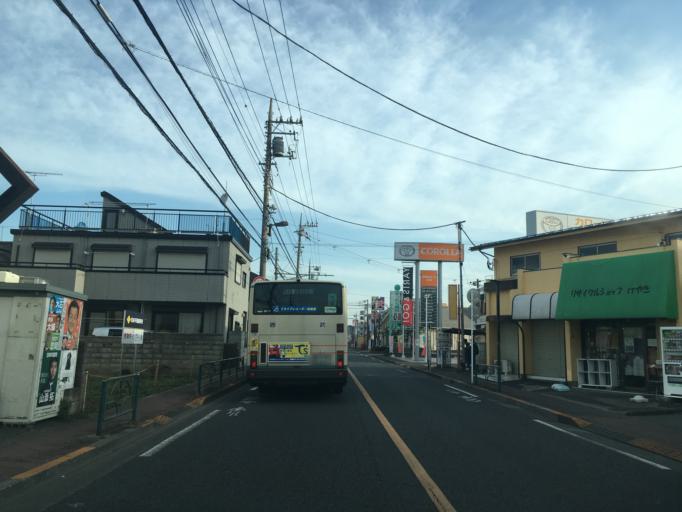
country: JP
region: Tokyo
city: Kokubunji
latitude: 35.7137
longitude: 139.4290
